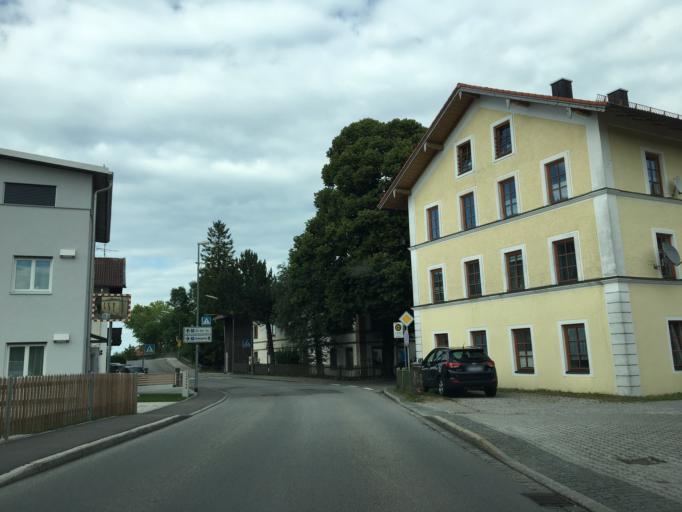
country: DE
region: Bavaria
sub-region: Upper Bavaria
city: Holzkirchen
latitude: 47.8791
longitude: 11.7014
